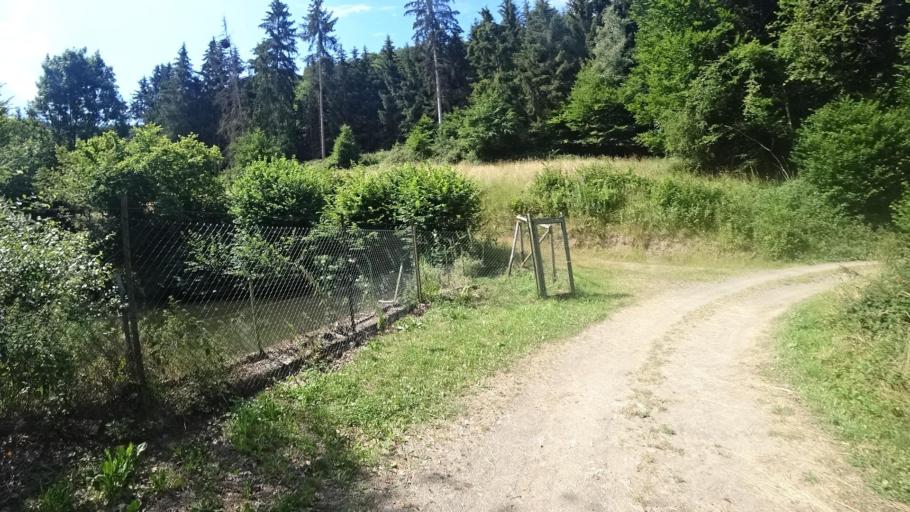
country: DE
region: Rheinland-Pfalz
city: Heckenbach
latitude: 50.4773
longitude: 7.0442
